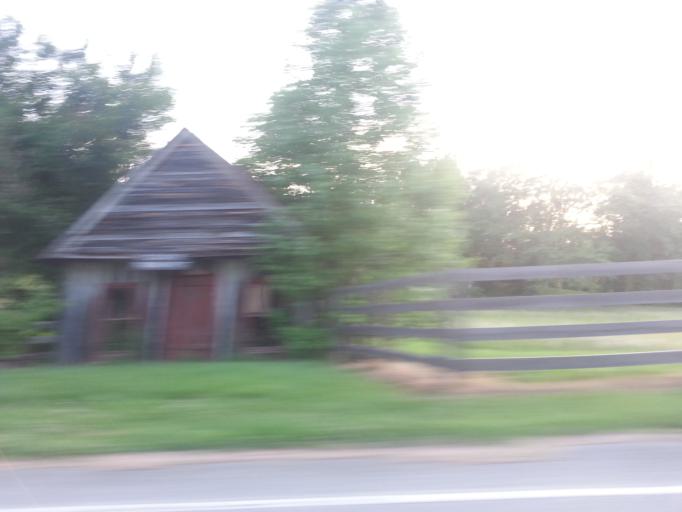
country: US
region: Tennessee
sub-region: McMinn County
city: Etowah
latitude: 35.2628
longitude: -84.2875
